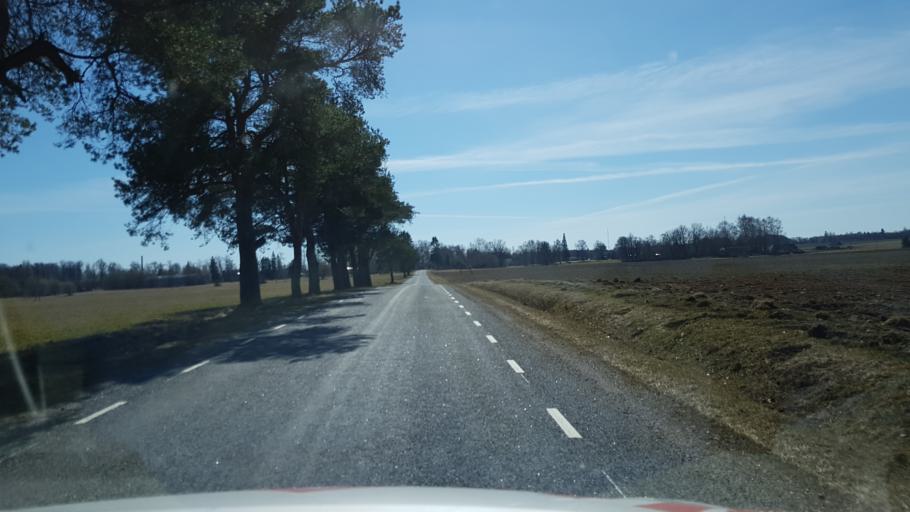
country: EE
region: Laeaene-Virumaa
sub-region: Vinni vald
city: Vinni
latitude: 59.1041
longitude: 26.5258
